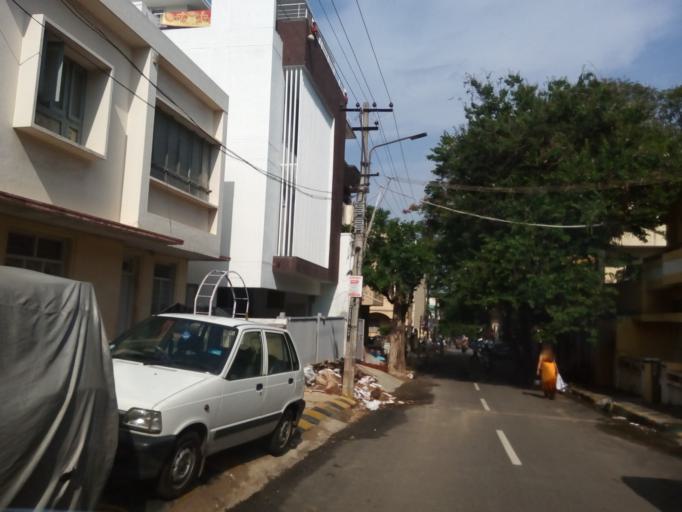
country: IN
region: Karnataka
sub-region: Bangalore Urban
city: Bangalore
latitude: 13.0054
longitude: 77.5774
